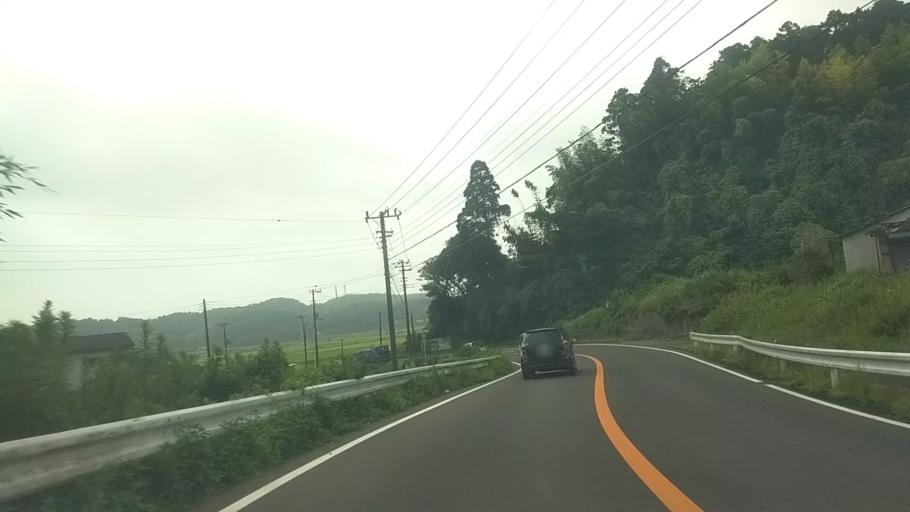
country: JP
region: Chiba
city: Ohara
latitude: 35.2647
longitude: 140.3717
